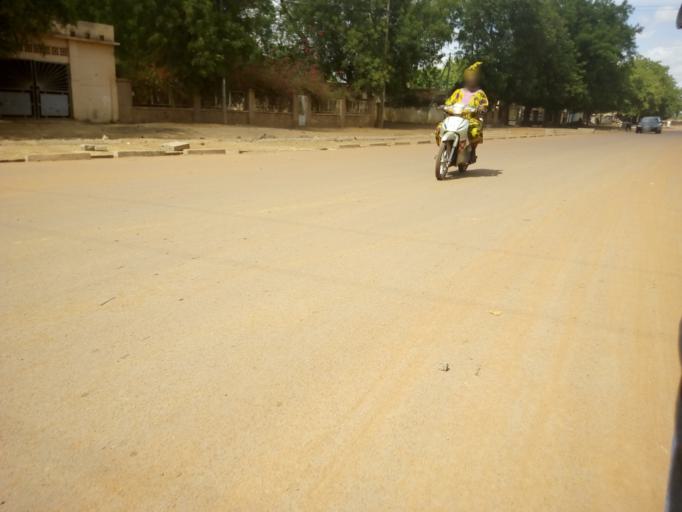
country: ML
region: Segou
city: Segou
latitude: 13.4423
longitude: -6.2440
